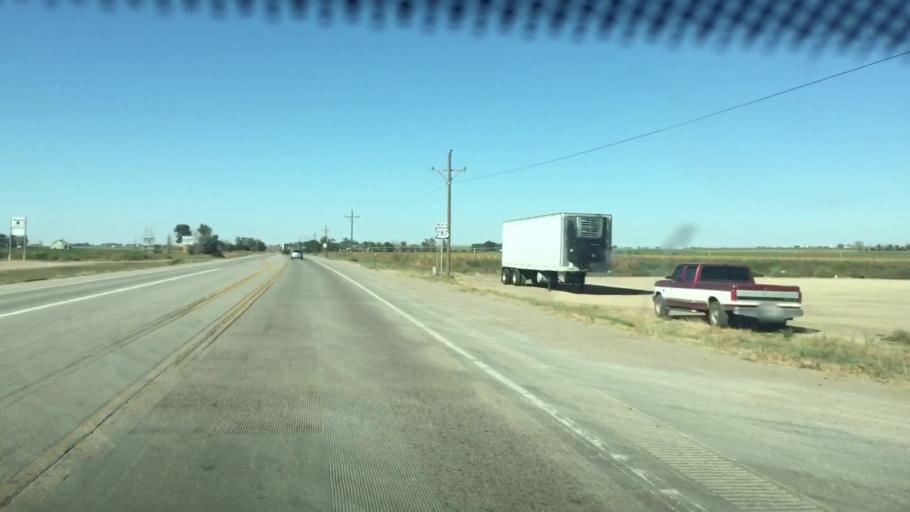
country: US
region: Colorado
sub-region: Prowers County
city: Lamar
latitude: 38.1589
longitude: -102.7237
